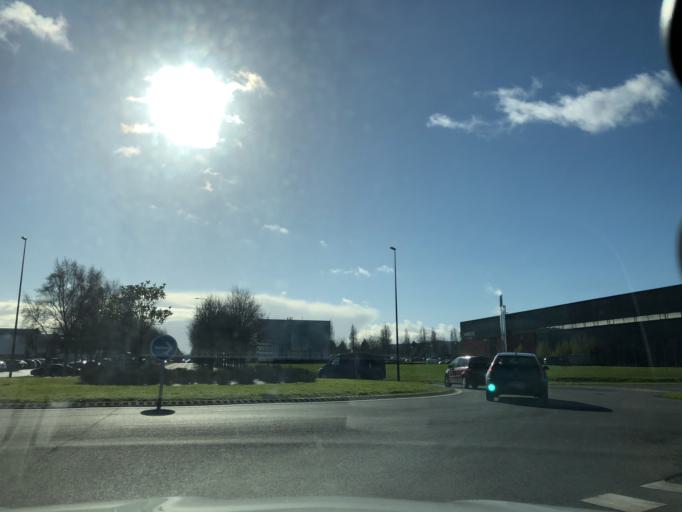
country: FR
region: Lower Normandy
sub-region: Departement du Calvados
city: Epron
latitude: 49.2180
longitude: -0.3541
